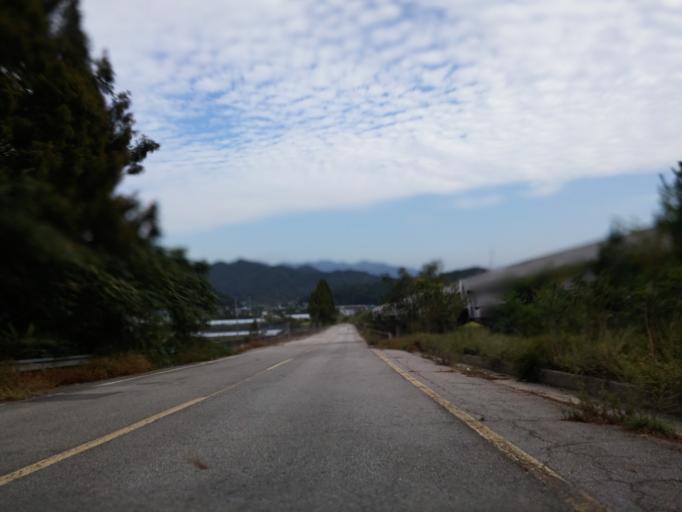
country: KR
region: Chungcheongnam-do
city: Yonmu
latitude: 36.1630
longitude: 127.1975
